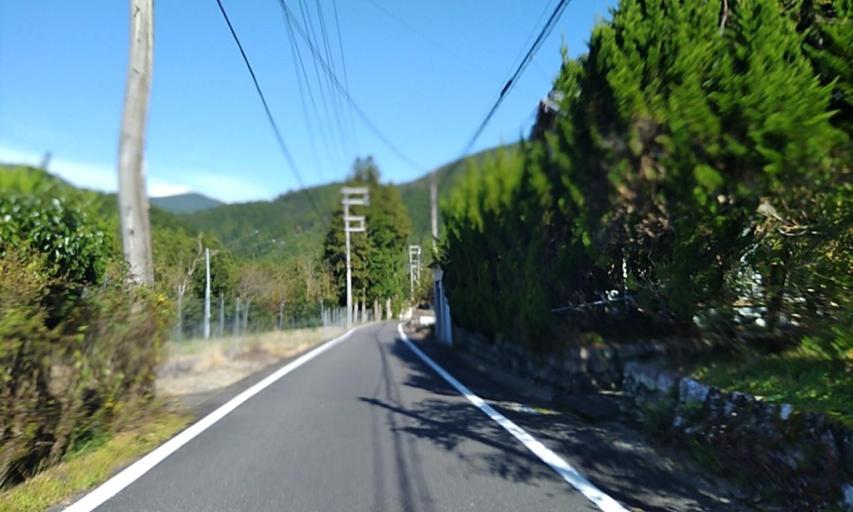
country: JP
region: Wakayama
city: Shingu
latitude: 33.9285
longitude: 135.9796
